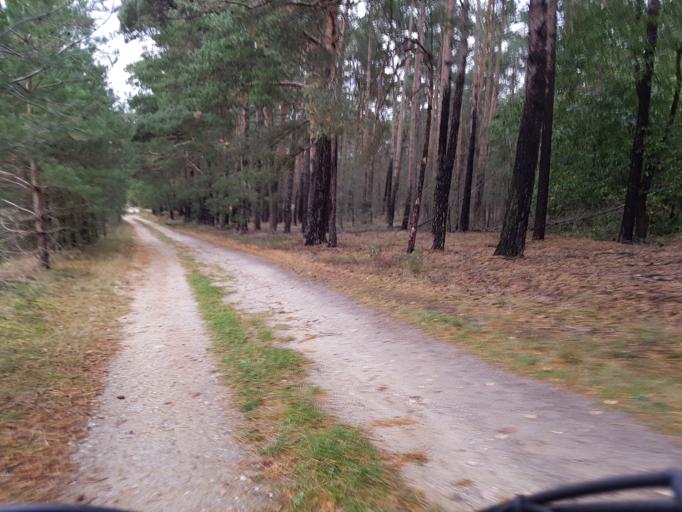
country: DE
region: Brandenburg
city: Schilda
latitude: 51.6135
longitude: 13.3931
